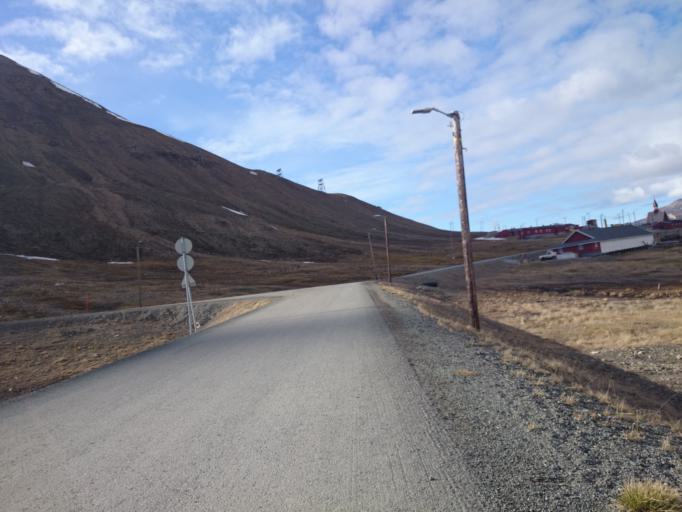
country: SJ
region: Svalbard
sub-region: Spitsbergen
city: Longyearbyen
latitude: 78.2170
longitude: 15.6239
